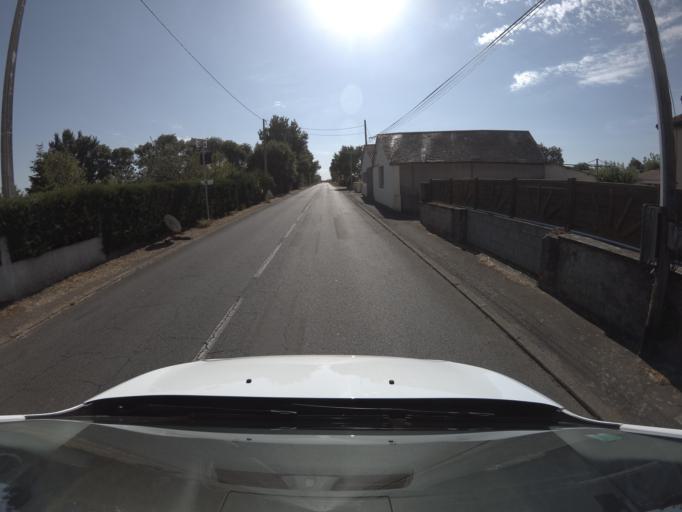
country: FR
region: Poitou-Charentes
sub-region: Departement des Deux-Sevres
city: Mauze-Thouarsais
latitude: 47.0066
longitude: -0.3465
